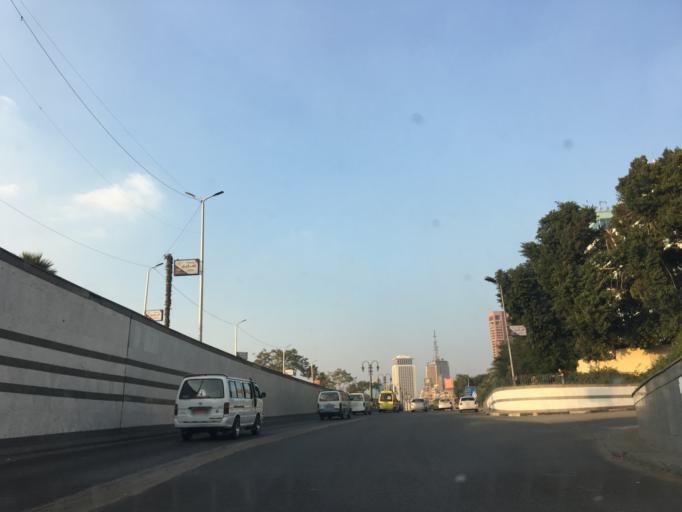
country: EG
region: Muhafazat al Qahirah
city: Cairo
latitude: 30.0443
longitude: 31.2319
